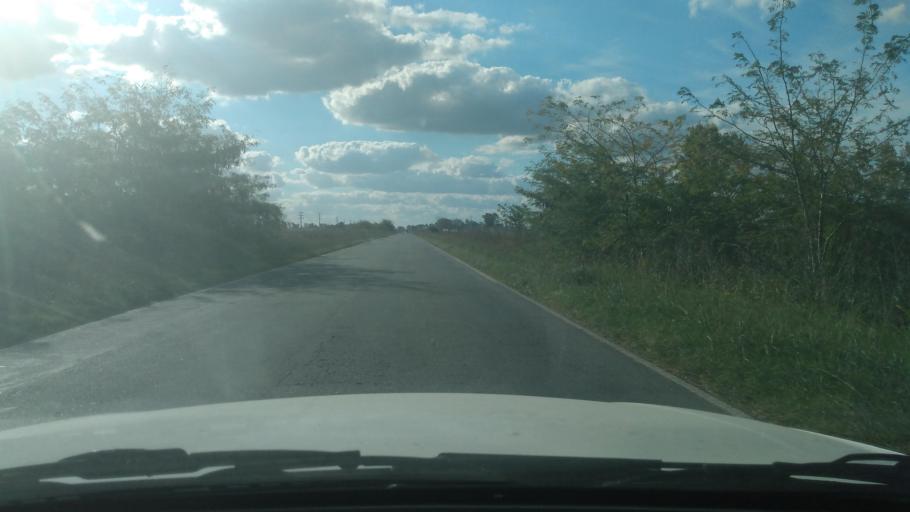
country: AR
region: Buenos Aires
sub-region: Partido de Mercedes
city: Mercedes
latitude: -34.7368
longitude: -59.3872
